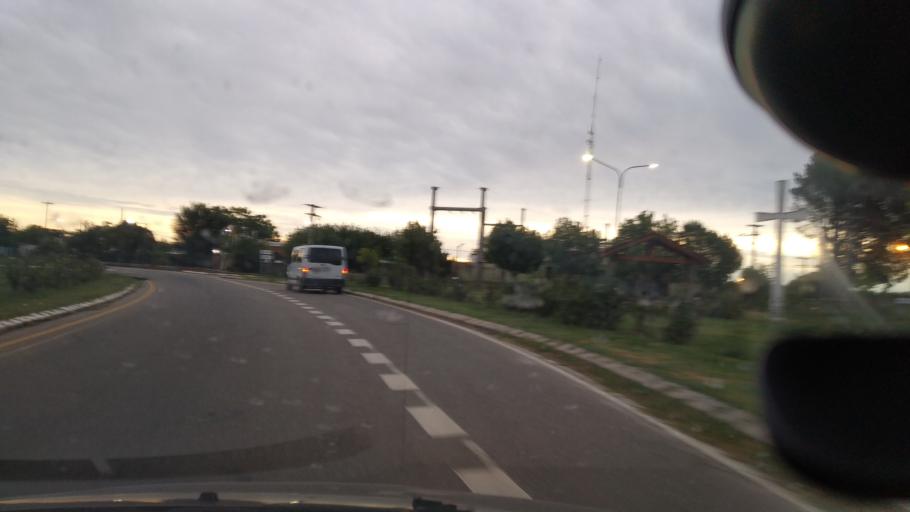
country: AR
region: Cordoba
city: Villa Las Rosas
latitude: -31.9119
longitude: -65.0341
